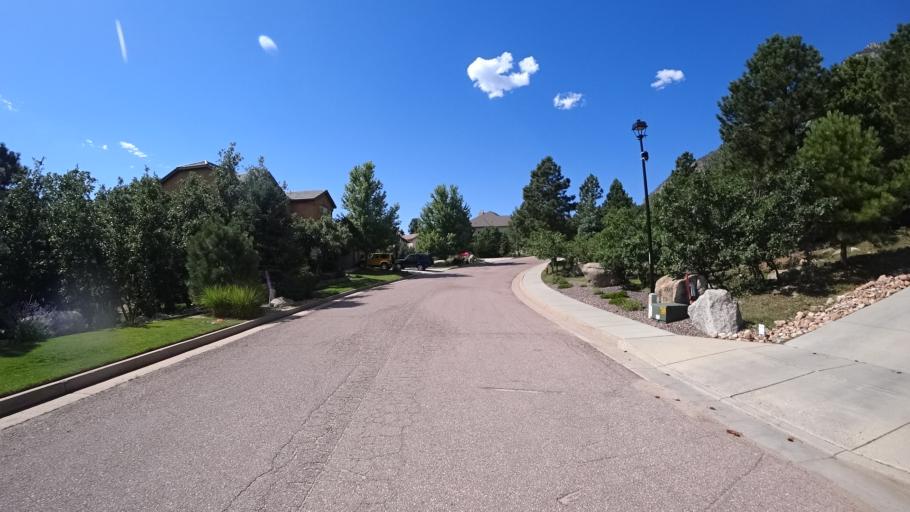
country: US
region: Colorado
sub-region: El Paso County
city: Fort Carson
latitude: 38.7458
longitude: -104.8356
